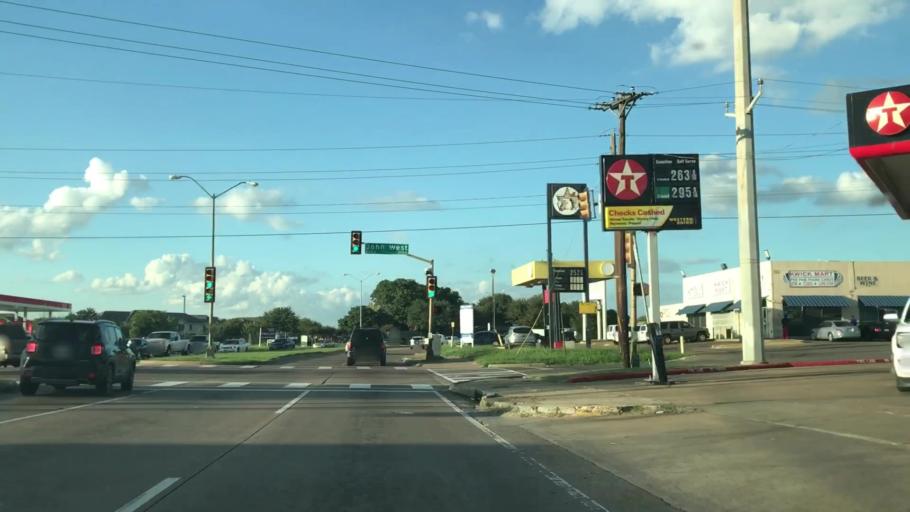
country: US
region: Texas
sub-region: Dallas County
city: Mesquite
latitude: 32.8068
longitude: -96.6681
